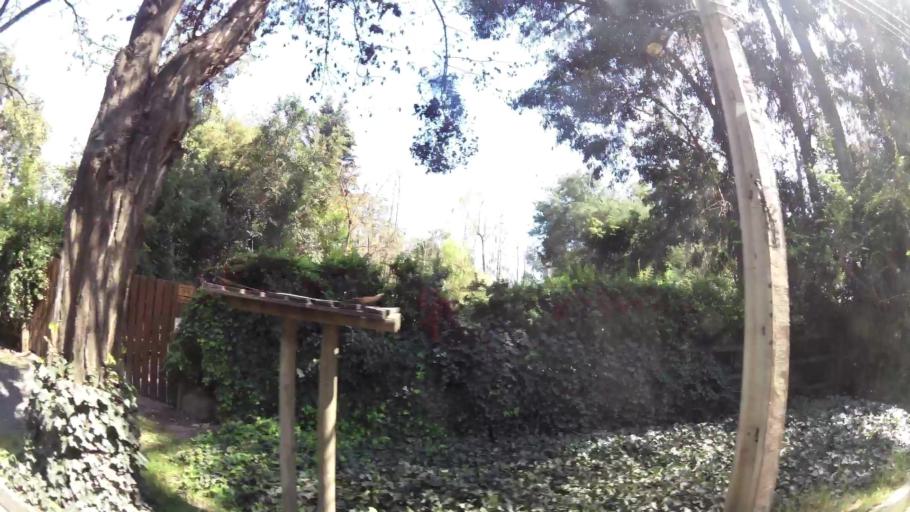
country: CL
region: Santiago Metropolitan
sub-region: Provincia de Santiago
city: Villa Presidente Frei, Nunoa, Santiago, Chile
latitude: -33.4408
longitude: -70.5245
